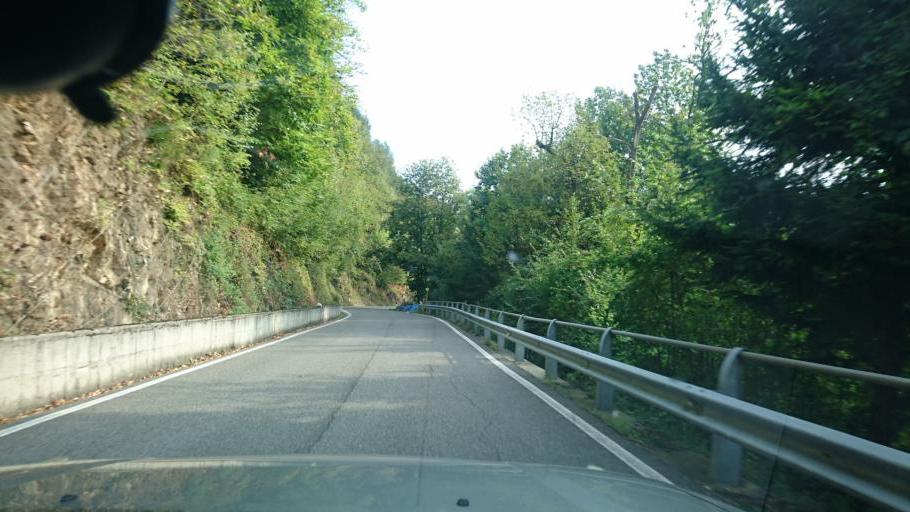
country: IT
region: Lombardy
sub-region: Provincia di Brescia
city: Paisco Loveno
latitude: 46.0810
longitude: 10.3012
